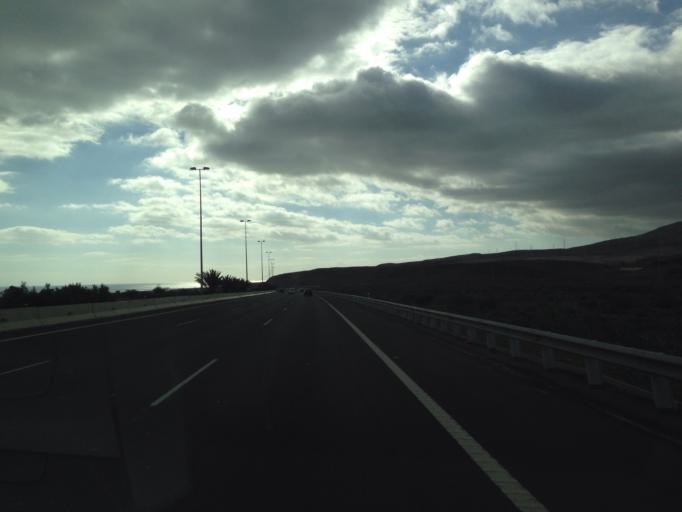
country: ES
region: Canary Islands
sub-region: Provincia de Las Palmas
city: Cruce de Arinaga
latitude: 27.8156
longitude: -15.4722
